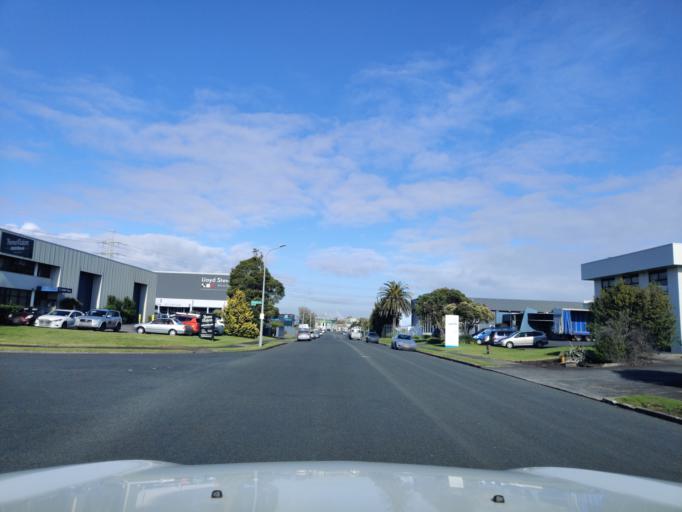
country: NZ
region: Auckland
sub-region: Auckland
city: Manukau City
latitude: -36.9387
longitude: 174.8822
